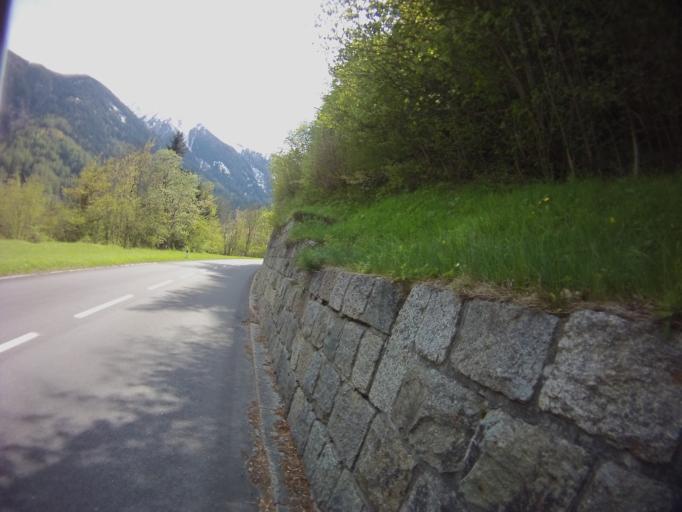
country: CH
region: Valais
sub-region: Martigny District
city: Martigny-Combe
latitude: 46.0741
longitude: 7.0282
